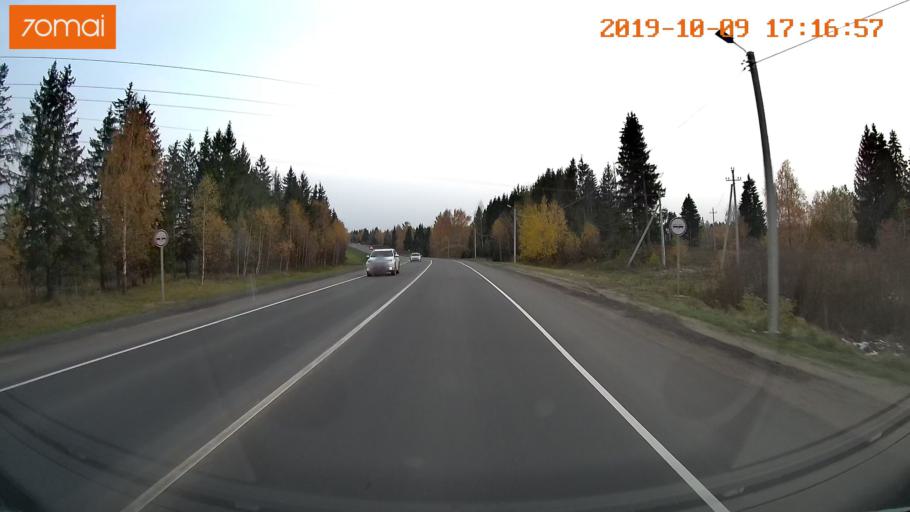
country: RU
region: Ivanovo
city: Furmanov
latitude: 57.2825
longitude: 41.1597
